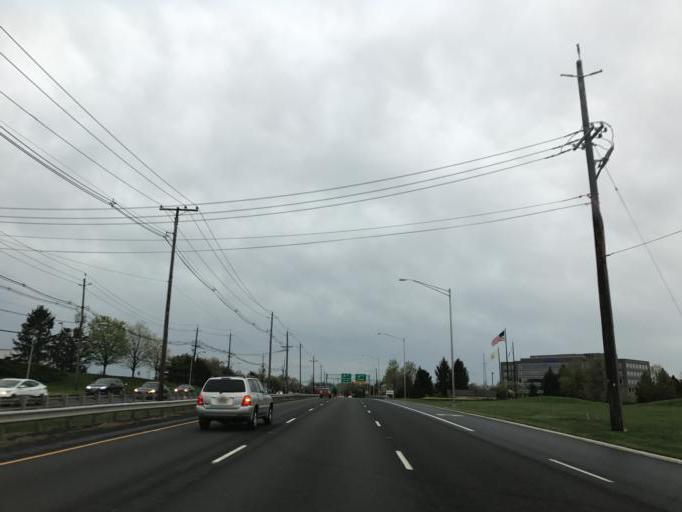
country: US
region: New Jersey
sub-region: Somerset County
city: Green Knoll
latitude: 40.5882
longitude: -74.6229
